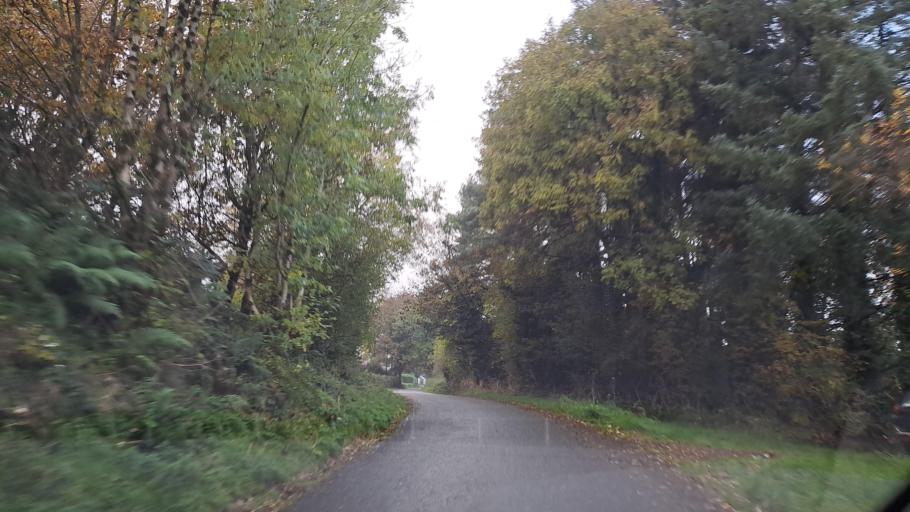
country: IE
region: Ulster
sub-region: An Cabhan
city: Kingscourt
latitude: 53.9706
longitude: -6.7984
